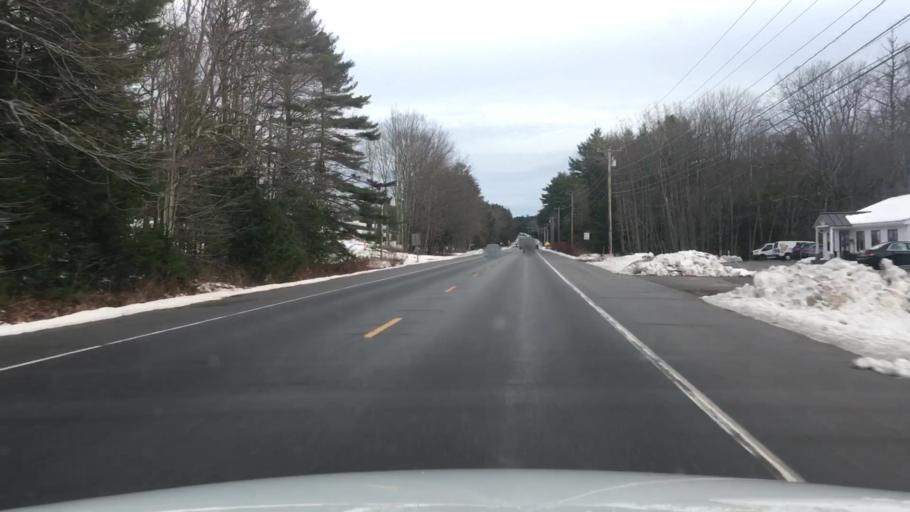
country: US
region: Maine
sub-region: Cumberland County
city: Falmouth Foreside
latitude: 43.7439
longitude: -70.2169
